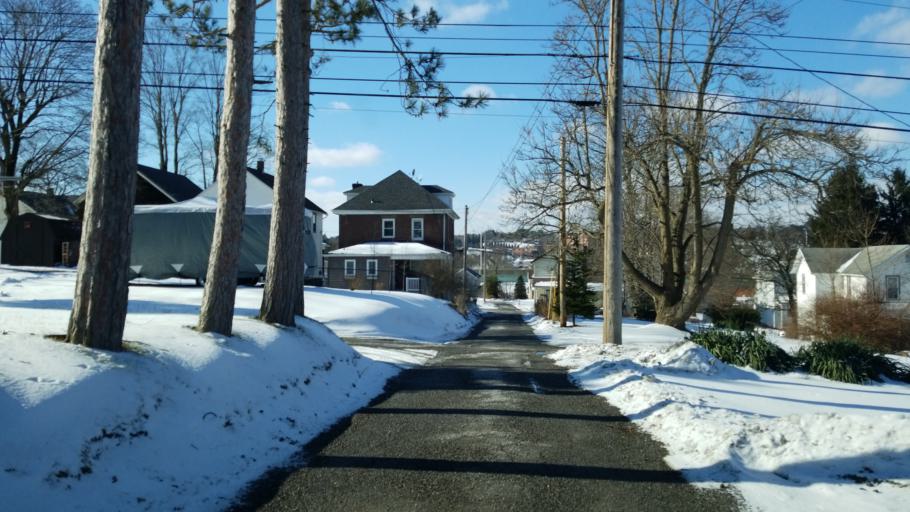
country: US
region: Pennsylvania
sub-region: Clearfield County
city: Sandy
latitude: 41.1117
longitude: -78.7670
